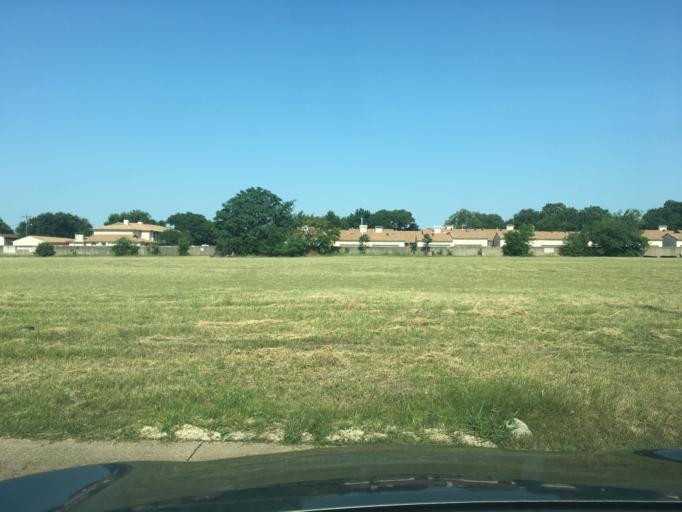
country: US
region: Texas
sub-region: Dallas County
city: Richardson
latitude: 32.9300
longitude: -96.6957
